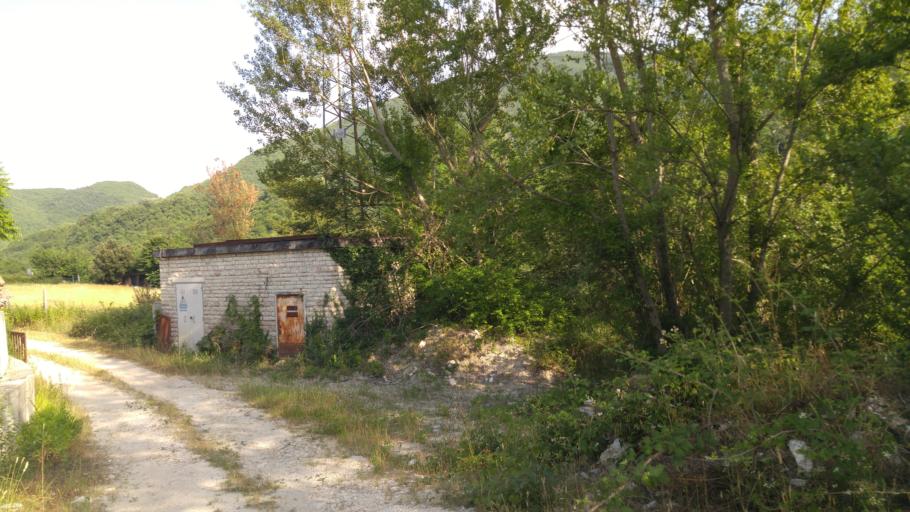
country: IT
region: The Marches
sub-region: Provincia di Pesaro e Urbino
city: Canavaccio
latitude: 43.6630
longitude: 12.7406
